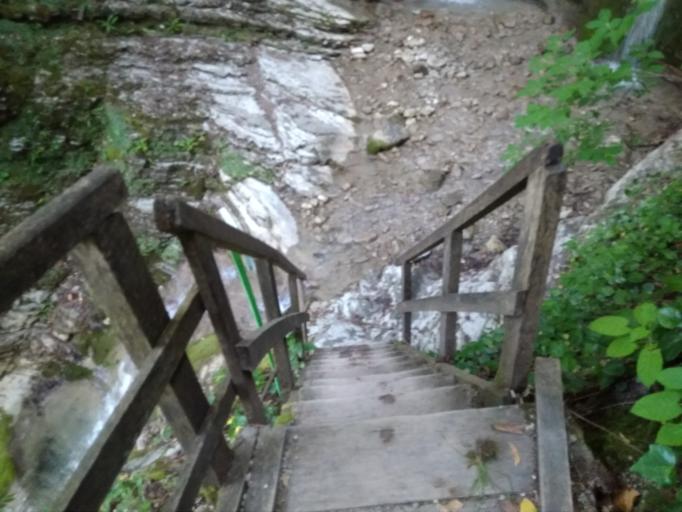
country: RU
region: Krasnodarskiy
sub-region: Sochi City
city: Lazarevskoye
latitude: 43.9986
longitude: 39.3969
